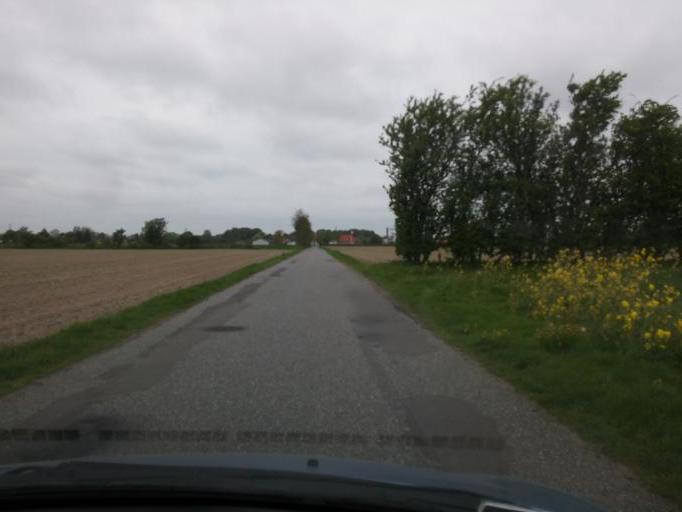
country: DK
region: South Denmark
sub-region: Odense Kommune
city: Bullerup
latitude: 55.4070
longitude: 10.5210
